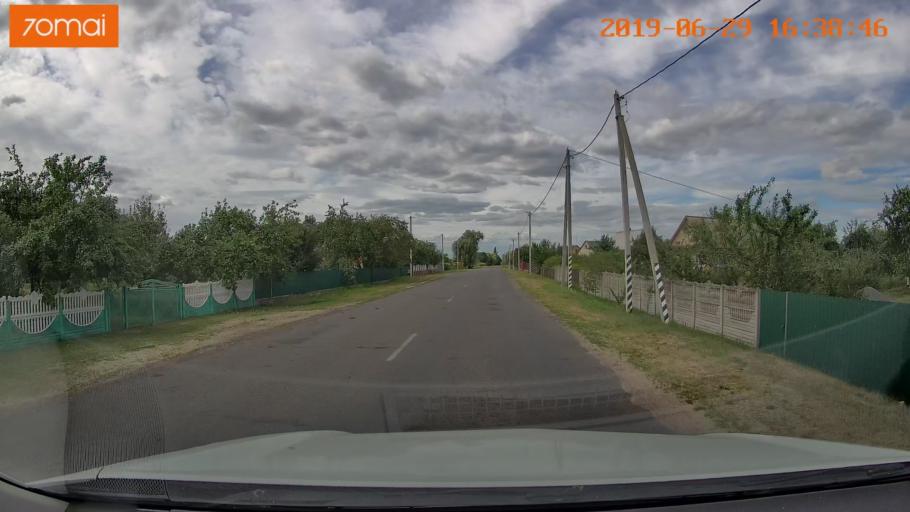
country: BY
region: Brest
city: Luninyets
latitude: 52.2354
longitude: 27.0153
